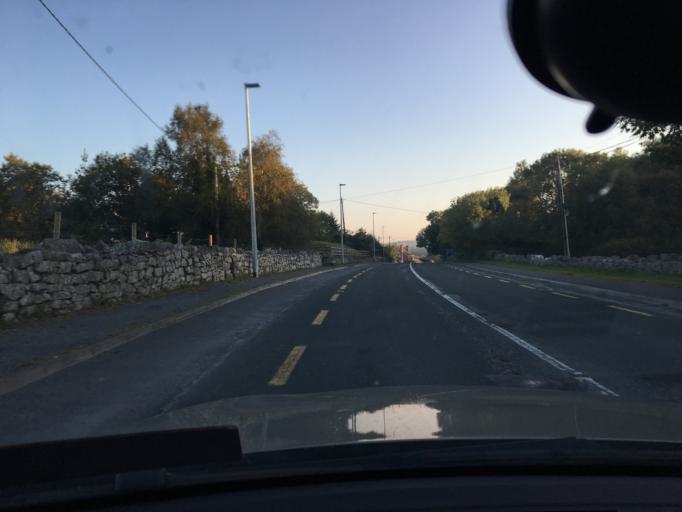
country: IE
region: Connaught
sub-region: County Galway
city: Moycullen
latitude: 53.3887
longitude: -9.2462
